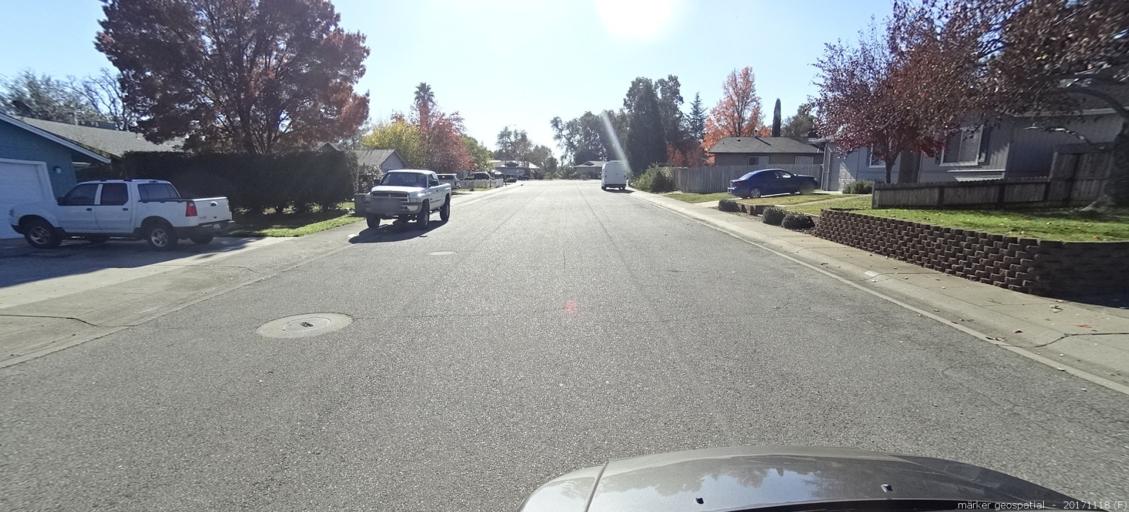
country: US
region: California
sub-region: Shasta County
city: Cottonwood
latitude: 40.3845
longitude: -122.2887
